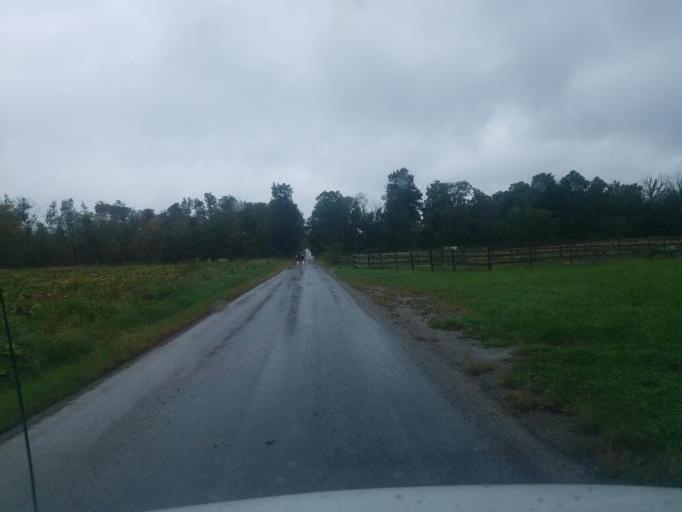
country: US
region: Ohio
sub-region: Wayne County
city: West Salem
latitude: 40.9378
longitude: -82.0418
